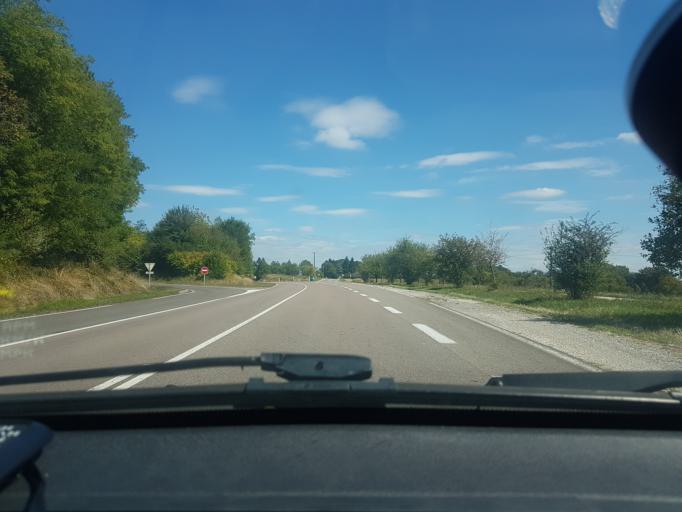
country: FR
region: Franche-Comte
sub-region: Departement de la Haute-Saone
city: Gray-la-Ville
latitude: 47.4154
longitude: 5.5146
